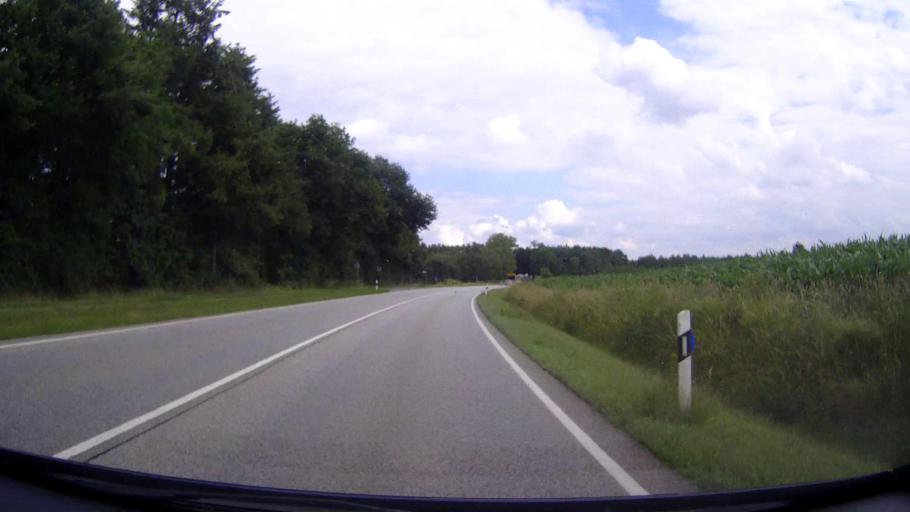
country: DE
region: Schleswig-Holstein
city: Arpsdorf
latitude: 54.0718
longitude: 9.8341
